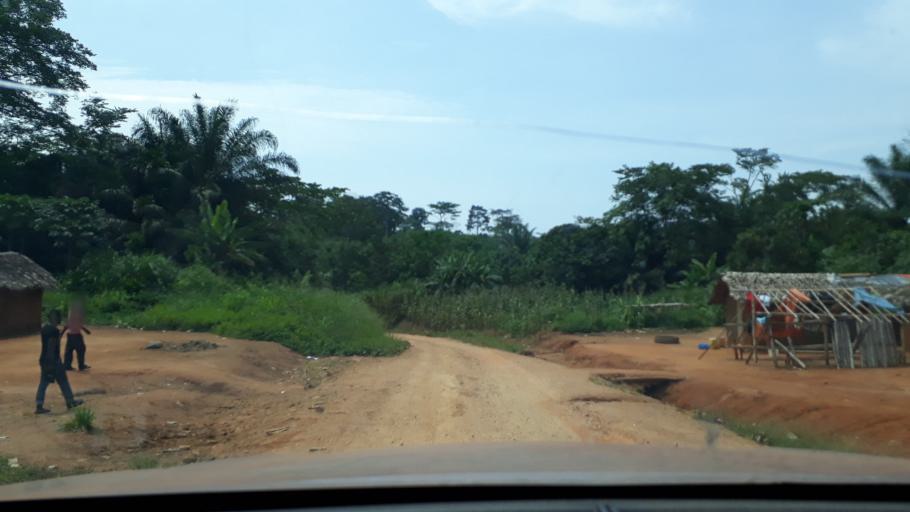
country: CD
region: Eastern Province
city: Wamba
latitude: 1.4120
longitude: 28.3806
